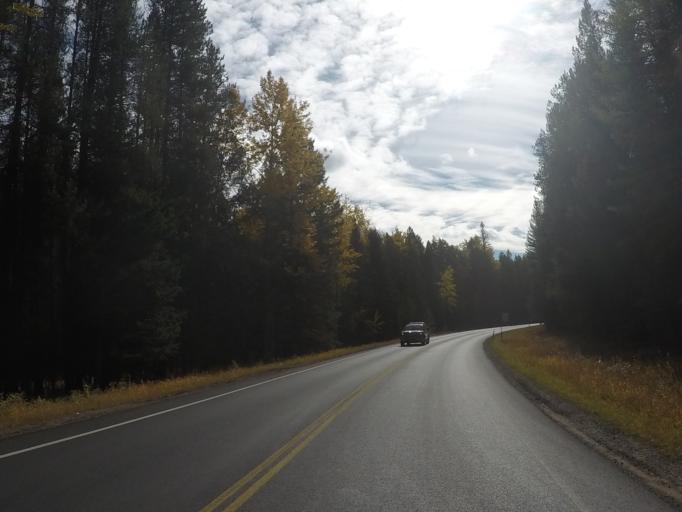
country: US
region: Montana
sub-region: Flathead County
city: Columbia Falls
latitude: 48.5108
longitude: -113.9864
